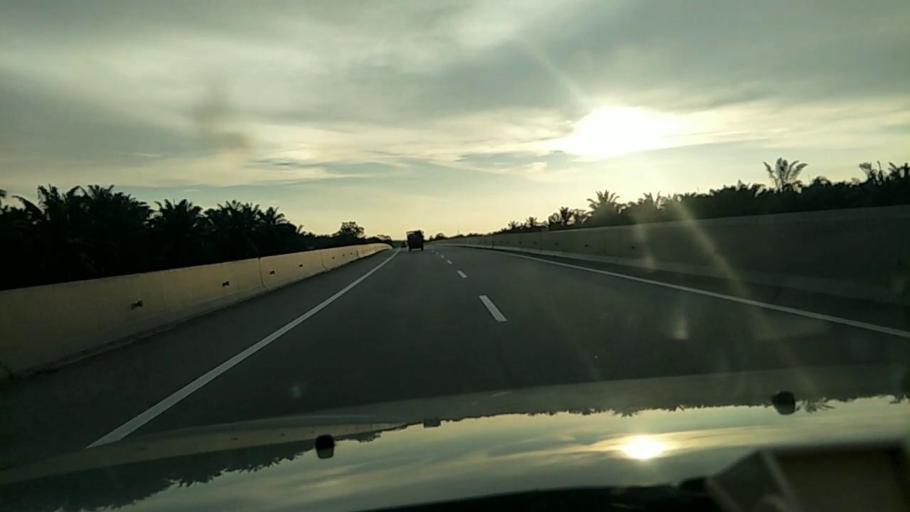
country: MY
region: Selangor
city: Batu Arang
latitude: 3.2886
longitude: 101.4327
